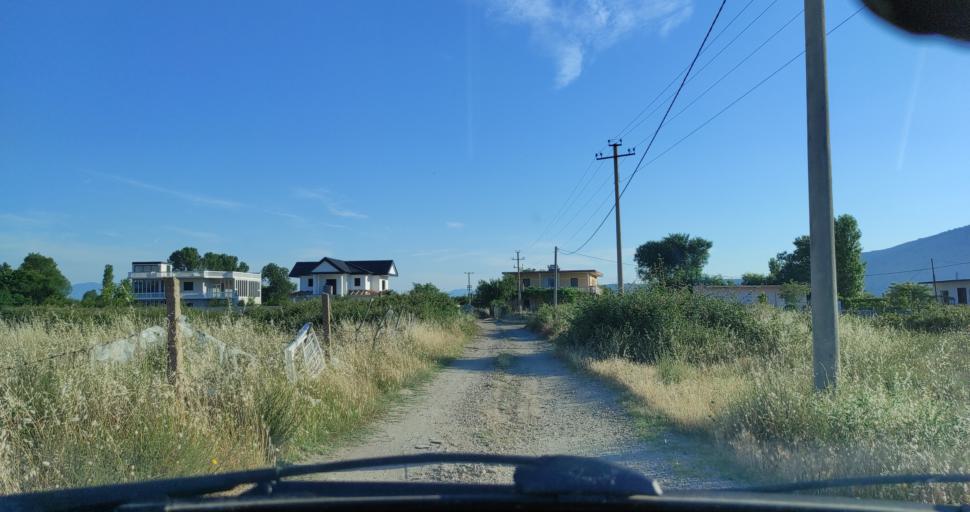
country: AL
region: Shkoder
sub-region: Rrethi i Shkodres
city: Velipoje
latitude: 41.8684
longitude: 19.4355
